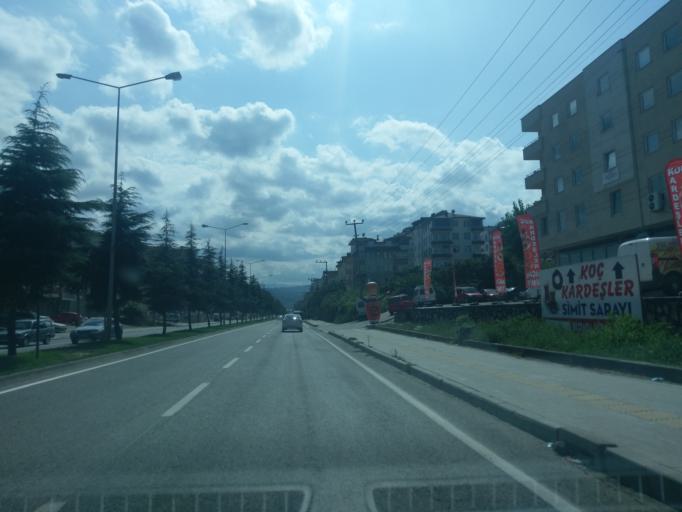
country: TR
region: Ordu
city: Ordu
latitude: 40.9643
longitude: 37.8998
